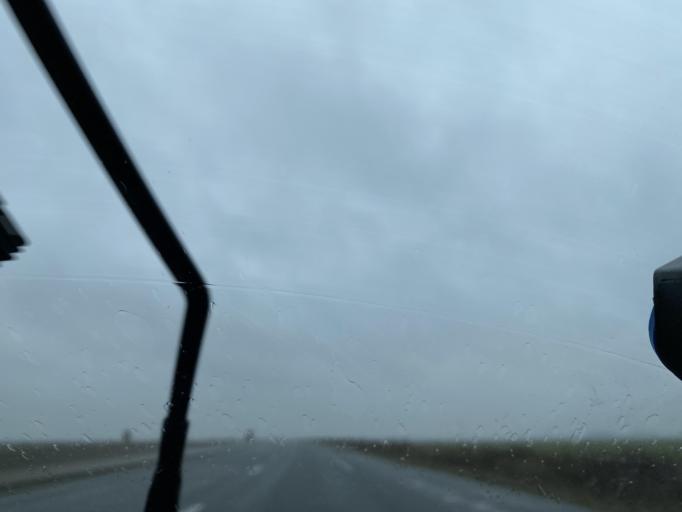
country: FR
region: Centre
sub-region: Departement d'Eure-et-Loir
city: Sours
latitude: 48.3704
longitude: 1.5913
